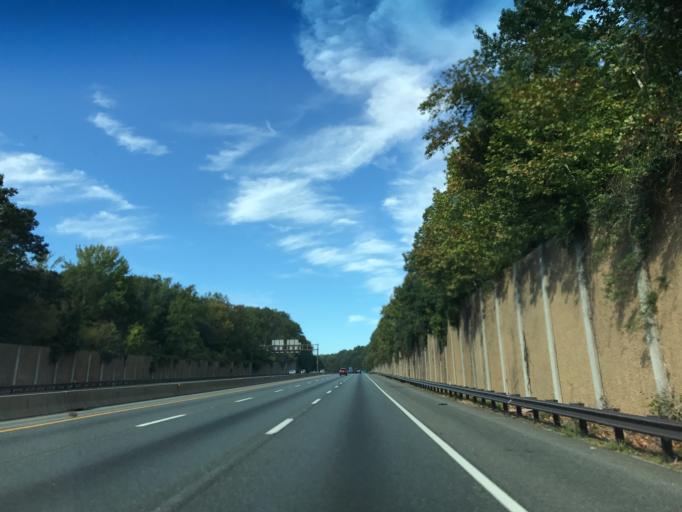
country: US
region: Maryland
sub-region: Anne Arundel County
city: Riva
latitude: 38.9841
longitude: -76.5923
